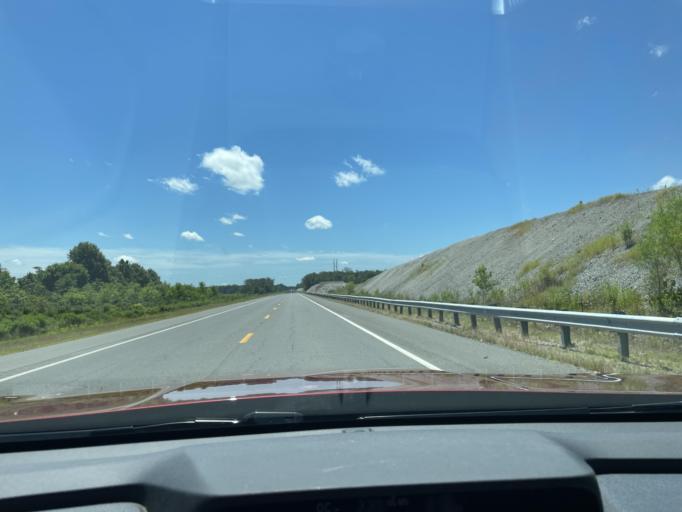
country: US
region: Arkansas
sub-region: Jefferson County
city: Pine Bluff
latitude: 34.1565
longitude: -91.9813
